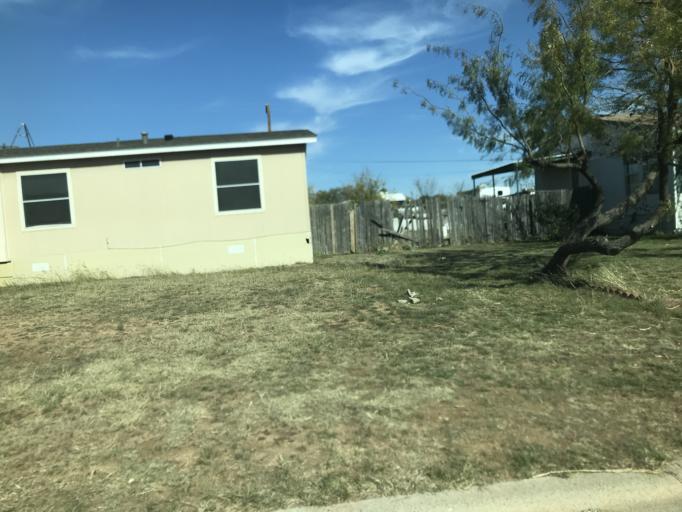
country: US
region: Texas
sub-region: Taylor County
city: Abilene
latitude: 32.5007
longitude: -99.7591
